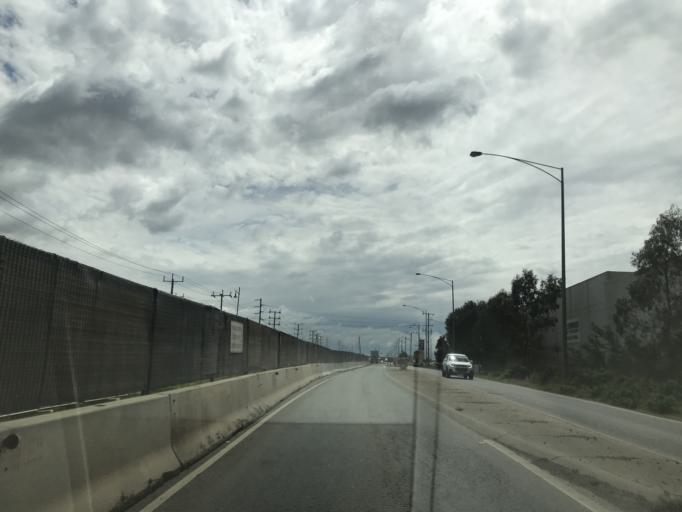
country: AU
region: Victoria
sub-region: Wyndham
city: Truganina
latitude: -37.8072
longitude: 144.7514
